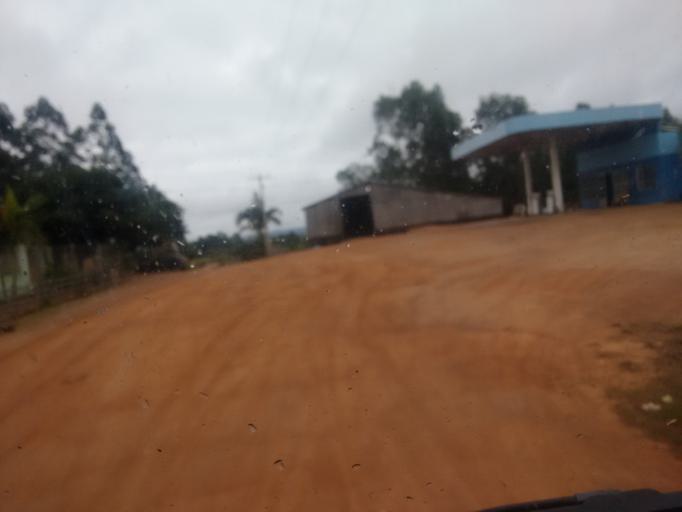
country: BR
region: Rio Grande do Sul
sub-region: Camaqua
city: Camaqua
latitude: -30.7264
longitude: -51.8485
